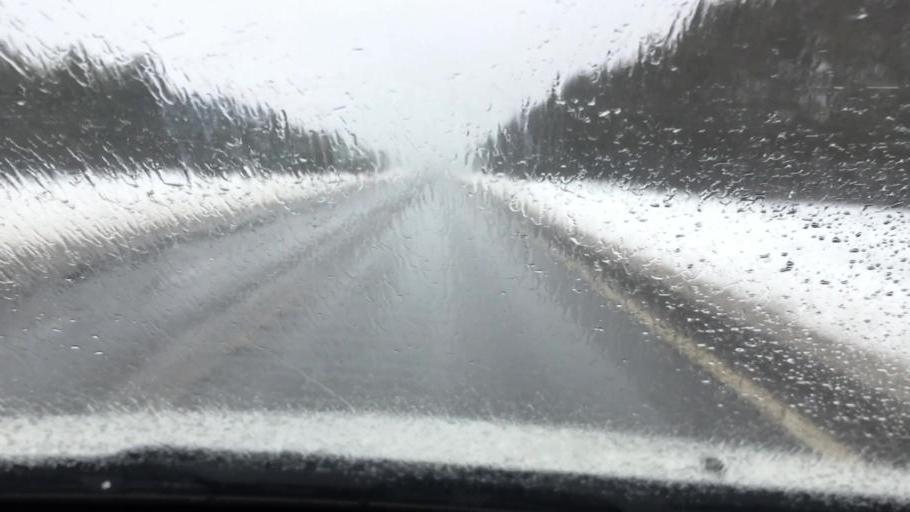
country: US
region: Michigan
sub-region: Antrim County
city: Mancelona
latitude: 44.9259
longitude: -85.0509
